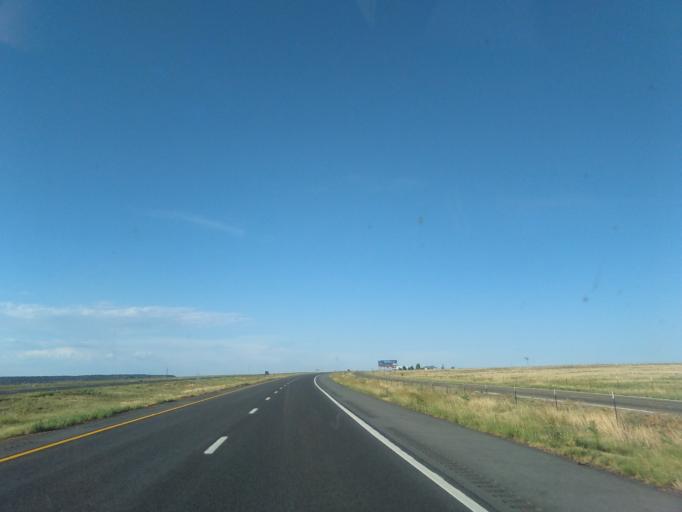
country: US
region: New Mexico
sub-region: San Miguel County
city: Las Vegas
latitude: 35.6656
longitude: -105.1844
